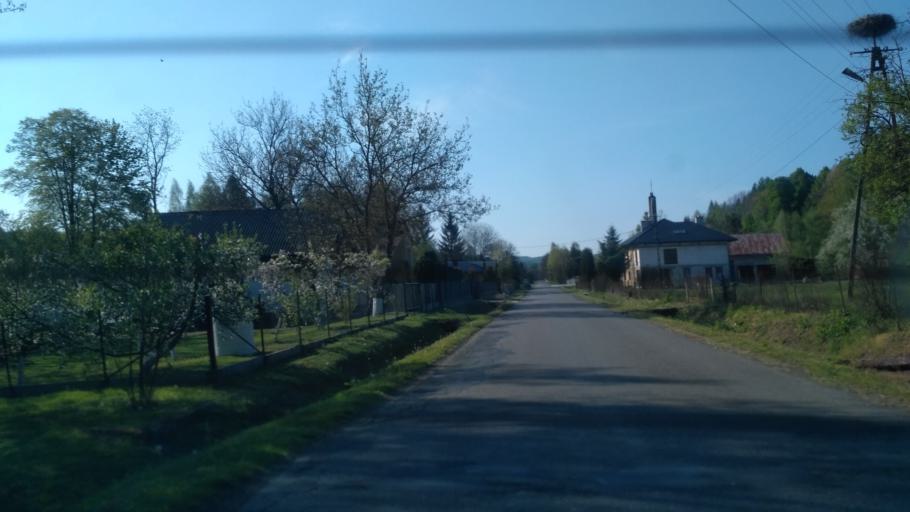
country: PL
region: Subcarpathian Voivodeship
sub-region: Powiat jaroslawski
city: Pruchnik
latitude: 49.8912
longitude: 22.5583
